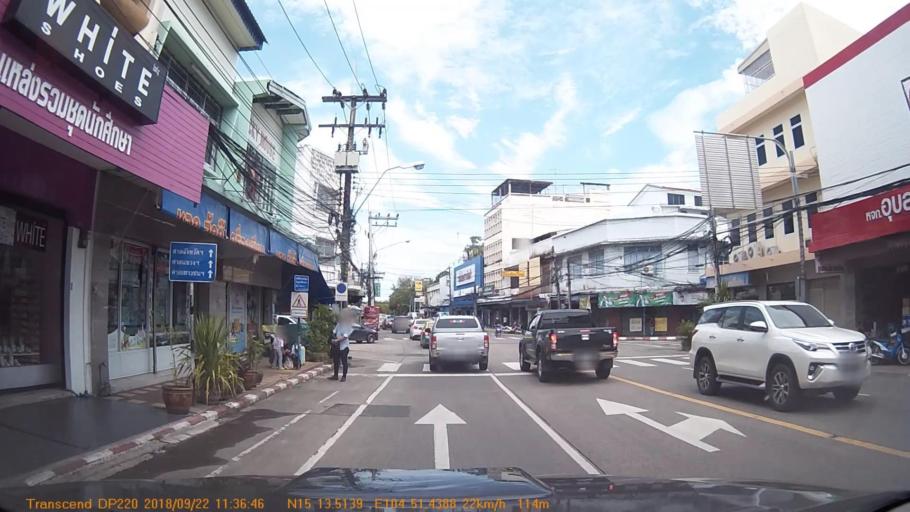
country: TH
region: Changwat Ubon Ratchathani
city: Ubon Ratchathani
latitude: 15.2253
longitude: 104.8573
